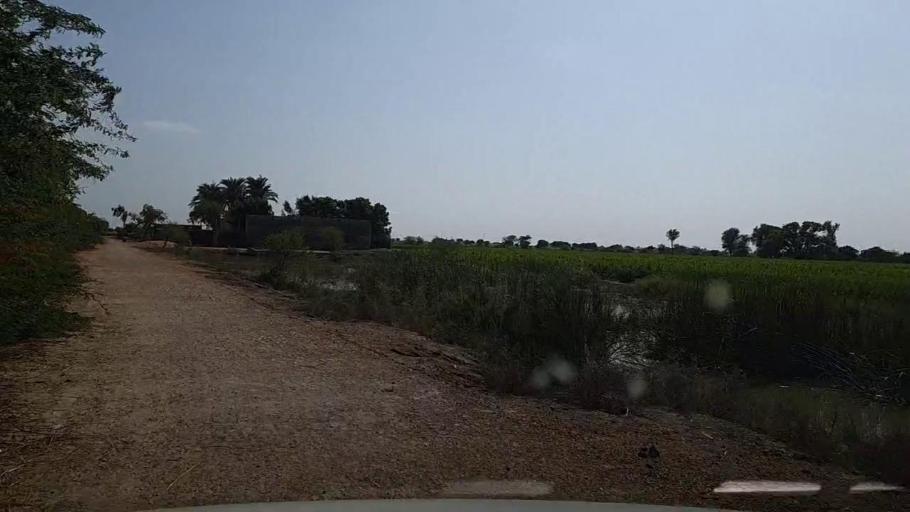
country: PK
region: Sindh
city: Kario
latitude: 24.8170
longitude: 68.5425
